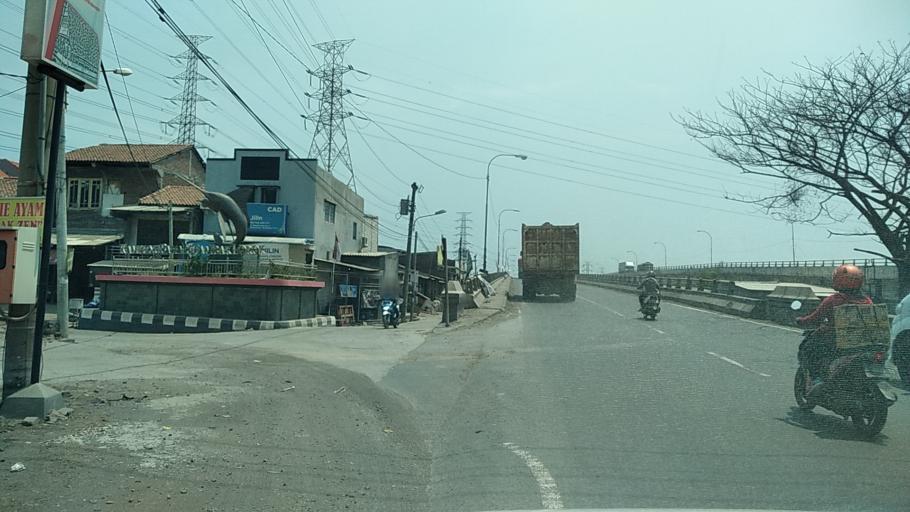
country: ID
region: Central Java
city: Semarang
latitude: -6.9508
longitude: 110.4388
